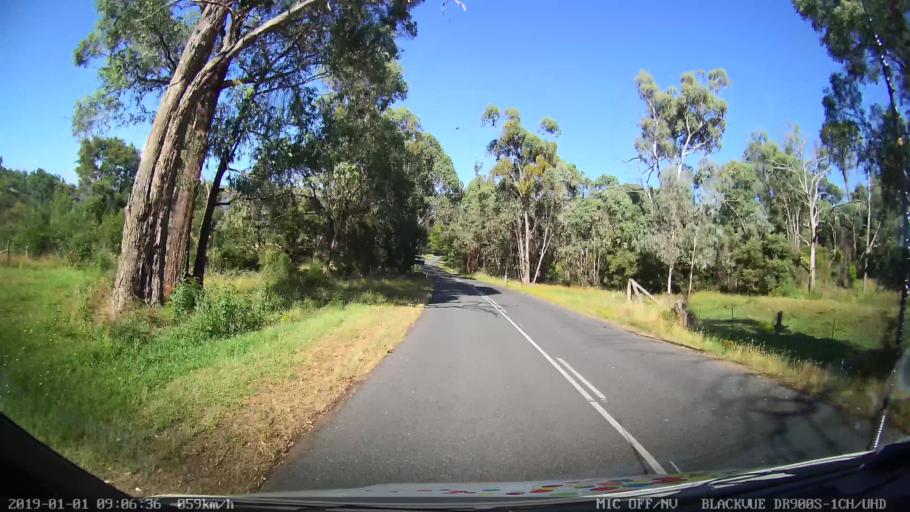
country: AU
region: New South Wales
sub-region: Snowy River
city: Jindabyne
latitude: -36.2168
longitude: 148.1364
